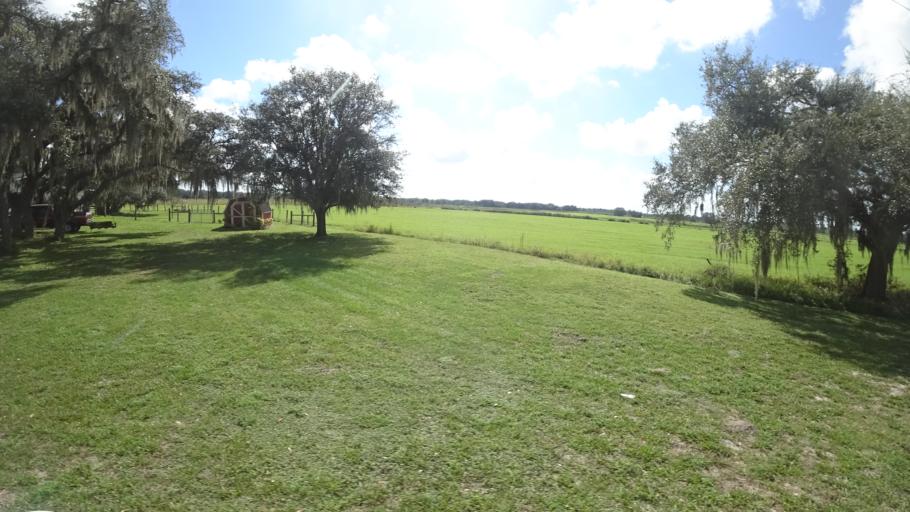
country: US
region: Florida
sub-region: Sarasota County
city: Lake Sarasota
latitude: 27.3664
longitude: -82.2216
